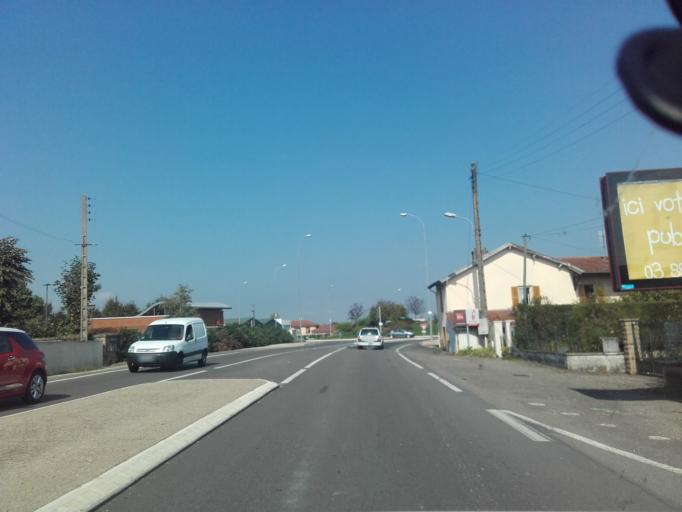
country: FR
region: Bourgogne
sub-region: Departement de Saone-et-Loire
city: Creches-sur-Saone
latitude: 46.2499
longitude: 4.7876
